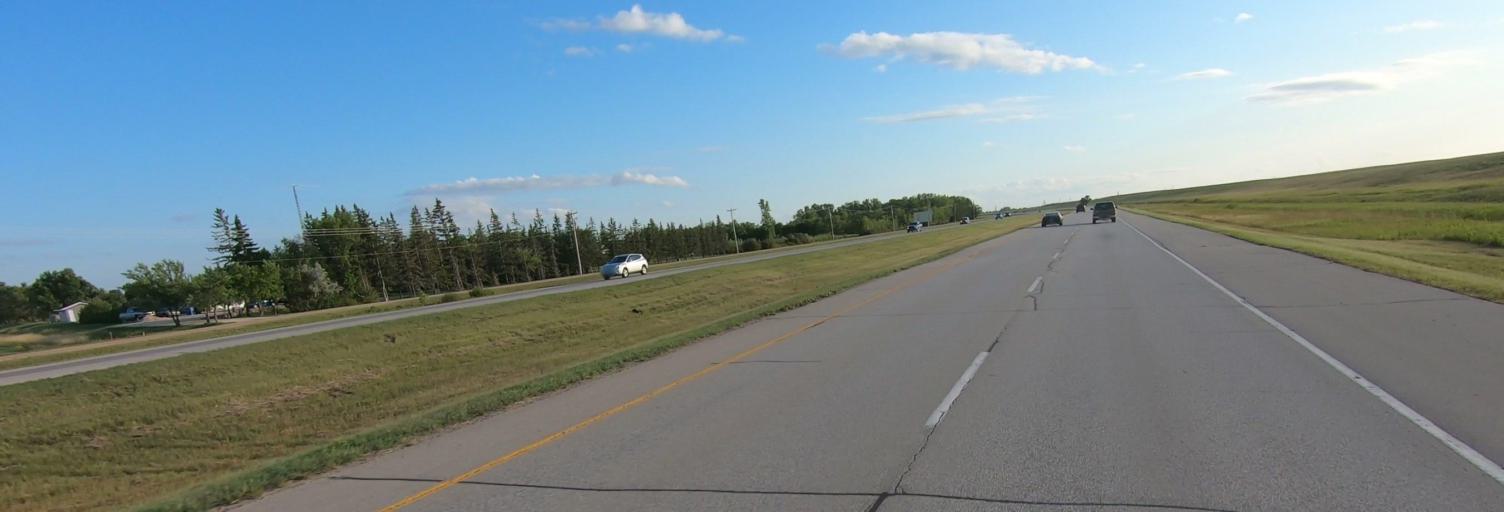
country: CA
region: Manitoba
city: Selkirk
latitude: 49.9973
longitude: -96.9706
